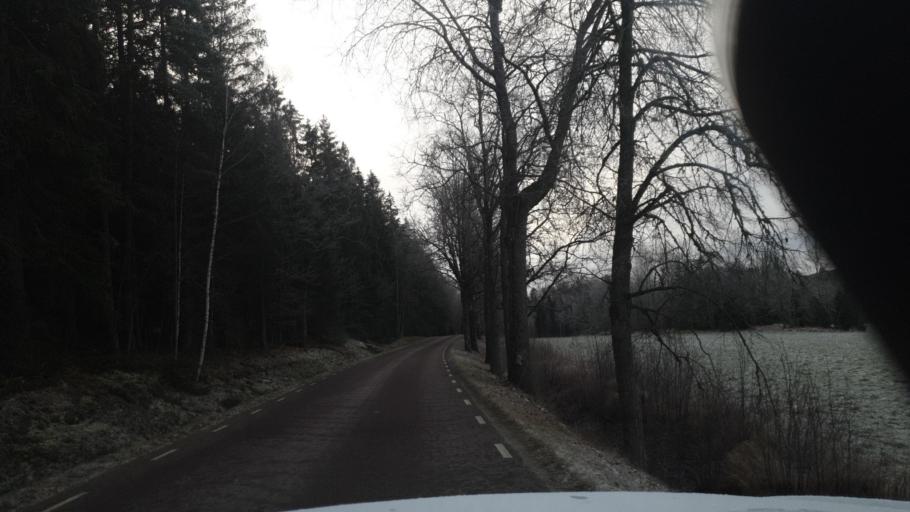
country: SE
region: Vaermland
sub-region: Karlstads Kommun
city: Valberg
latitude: 59.4354
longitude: 13.0874
